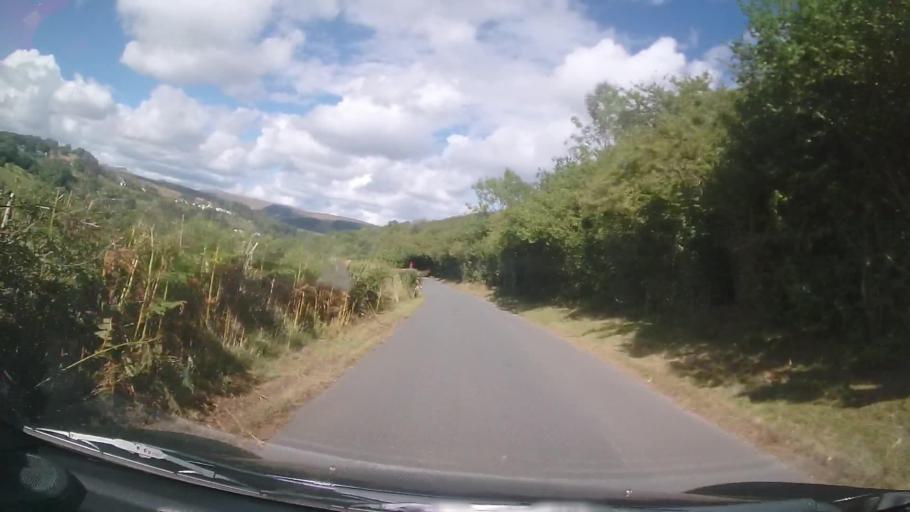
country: GB
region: Wales
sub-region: Merthyr Tydfil County Borough
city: Merthyr Tydfil
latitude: 51.7829
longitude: -3.3642
